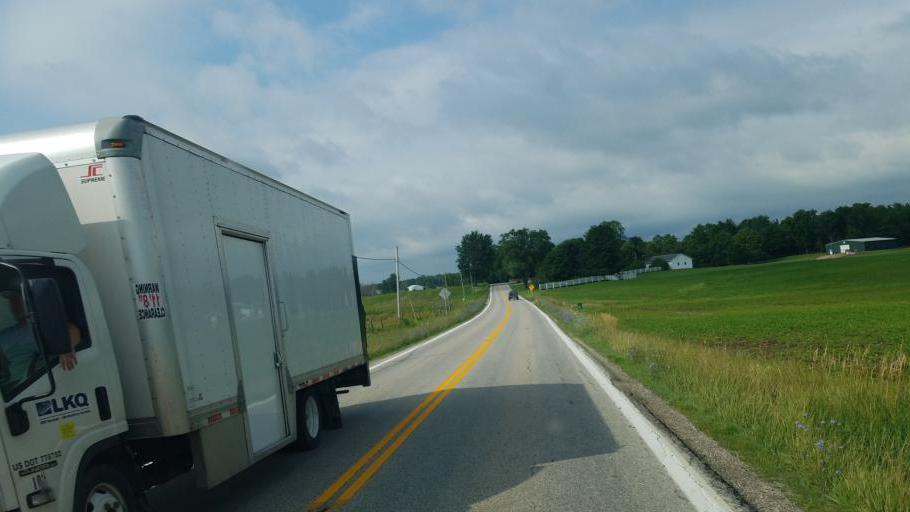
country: US
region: Ohio
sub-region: Knox County
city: Fredericktown
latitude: 40.4692
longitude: -82.6915
